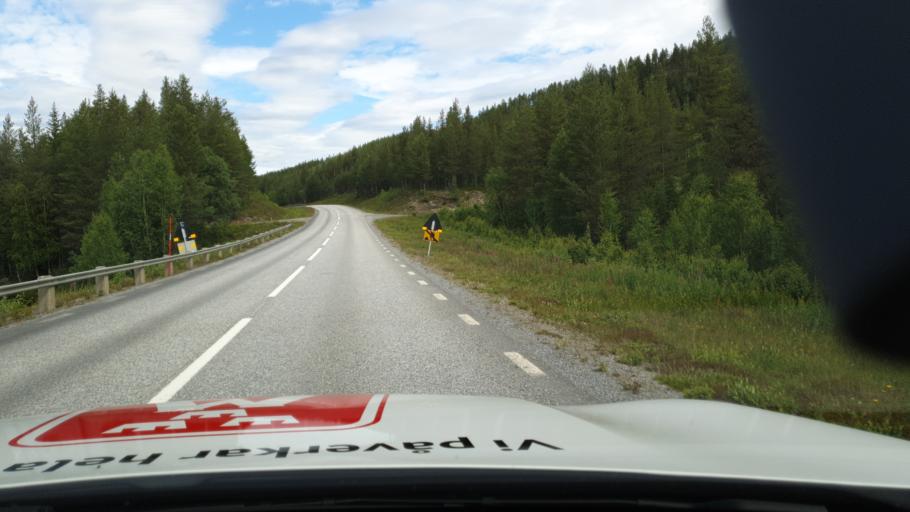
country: SE
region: Vaesterbotten
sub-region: Storumans Kommun
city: Fristad
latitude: 65.3777
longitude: 16.5141
